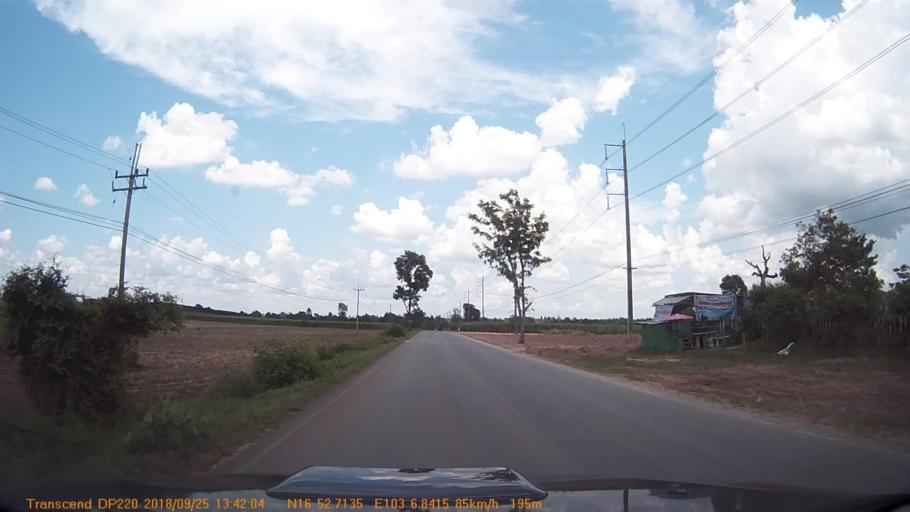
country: TH
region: Changwat Udon Thani
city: Si That
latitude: 16.8787
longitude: 103.1142
